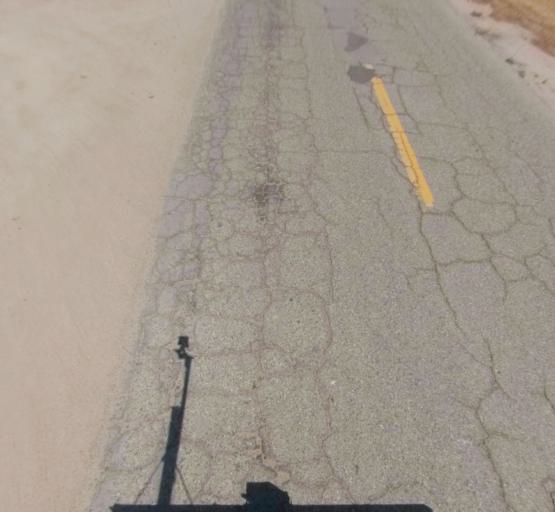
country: US
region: California
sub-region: Madera County
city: Chowchilla
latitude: 37.0860
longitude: -120.4370
